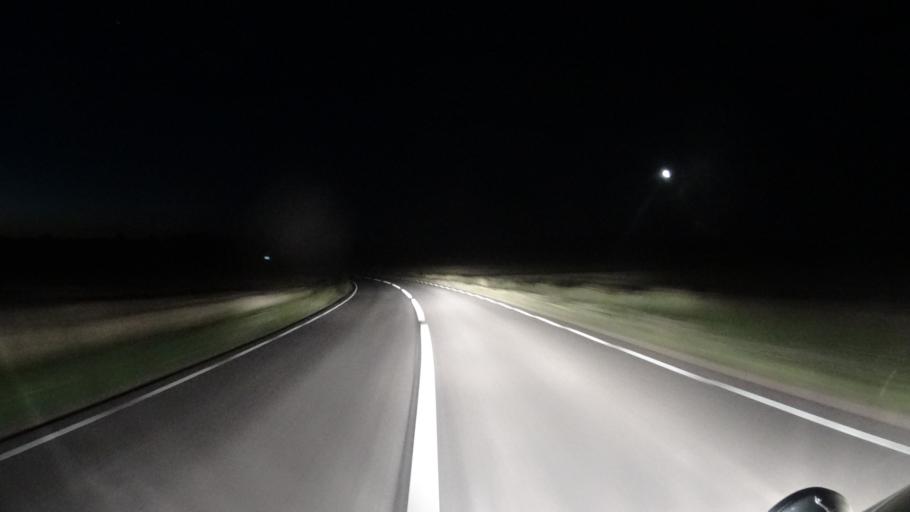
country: SE
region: OEstergoetland
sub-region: Odeshogs Kommun
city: OEdeshoeg
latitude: 58.2409
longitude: 14.7116
